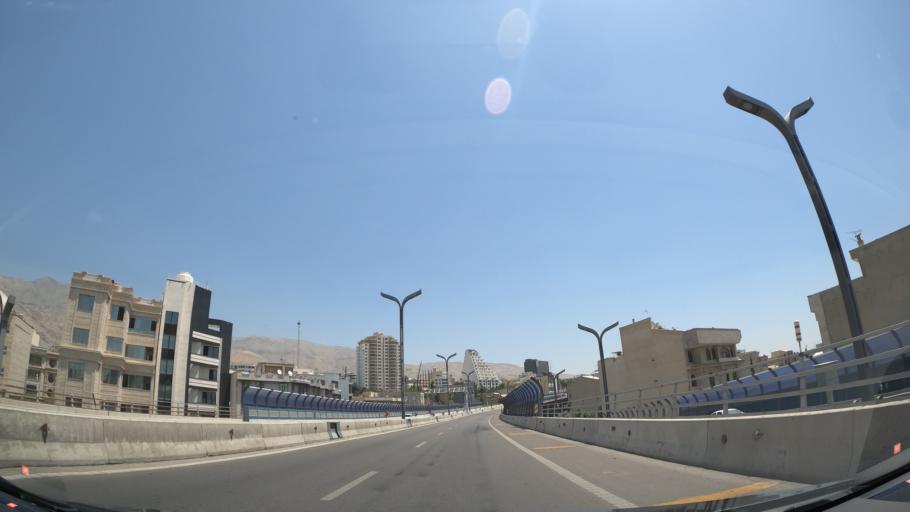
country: IR
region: Tehran
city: Tajrish
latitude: 35.7922
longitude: 51.4578
